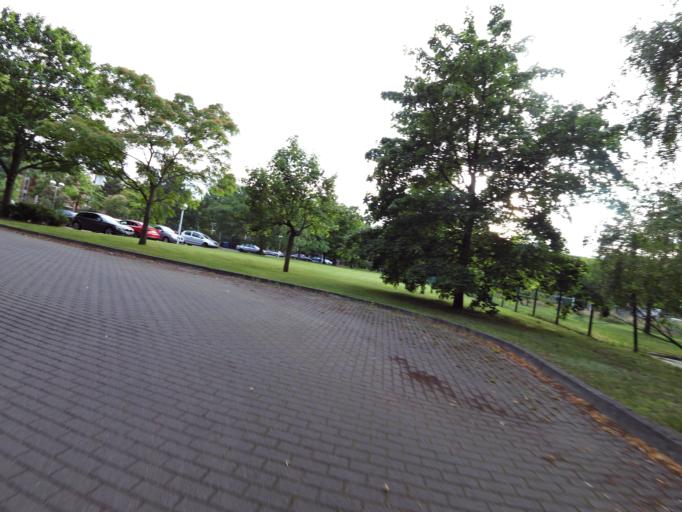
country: DE
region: Berlin
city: Lichterfelde
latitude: 52.4302
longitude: 13.3020
